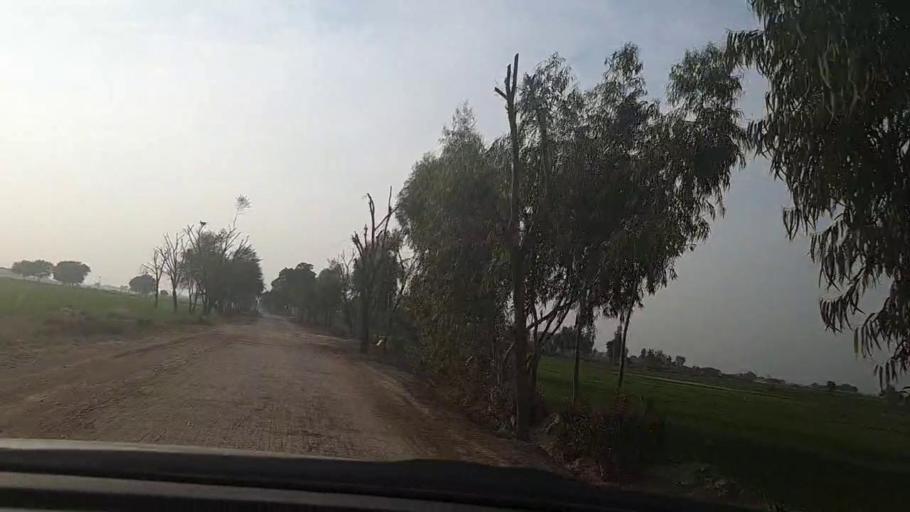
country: PK
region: Sindh
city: Daulatpur
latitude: 26.3369
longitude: 68.0282
